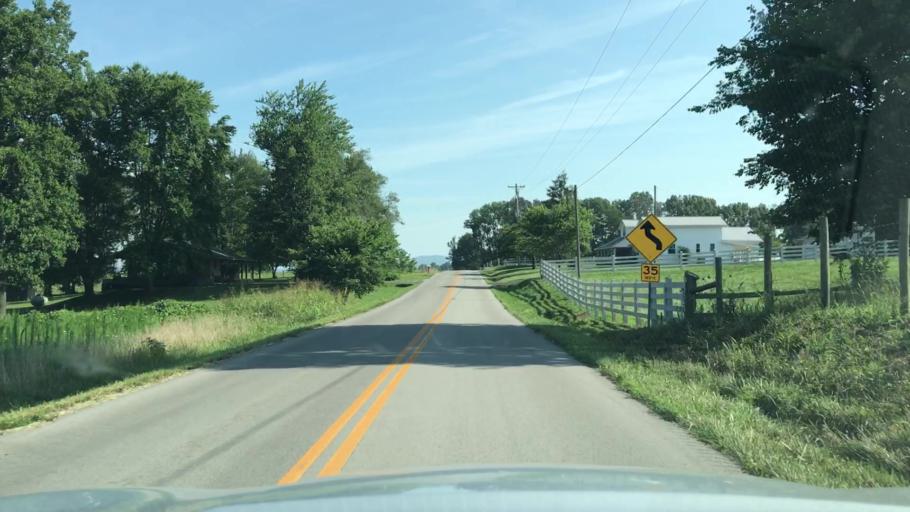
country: US
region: Tennessee
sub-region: Pickett County
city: Byrdstown
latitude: 36.6249
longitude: -85.0845
